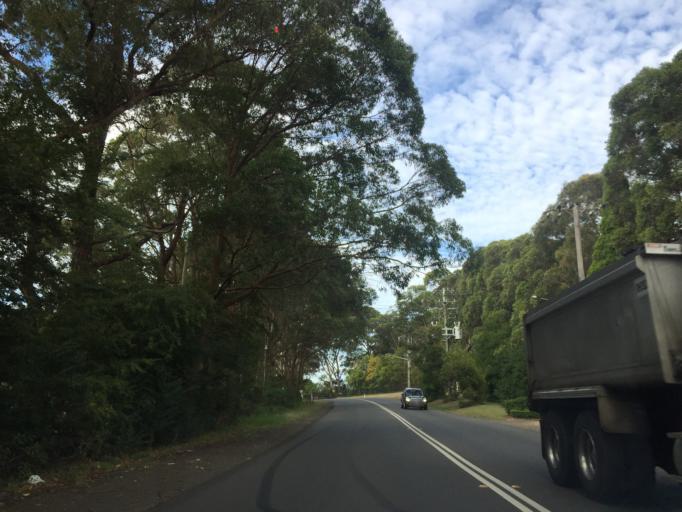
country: AU
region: New South Wales
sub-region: Hornsby Shire
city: Galston
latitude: -33.6528
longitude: 151.0561
